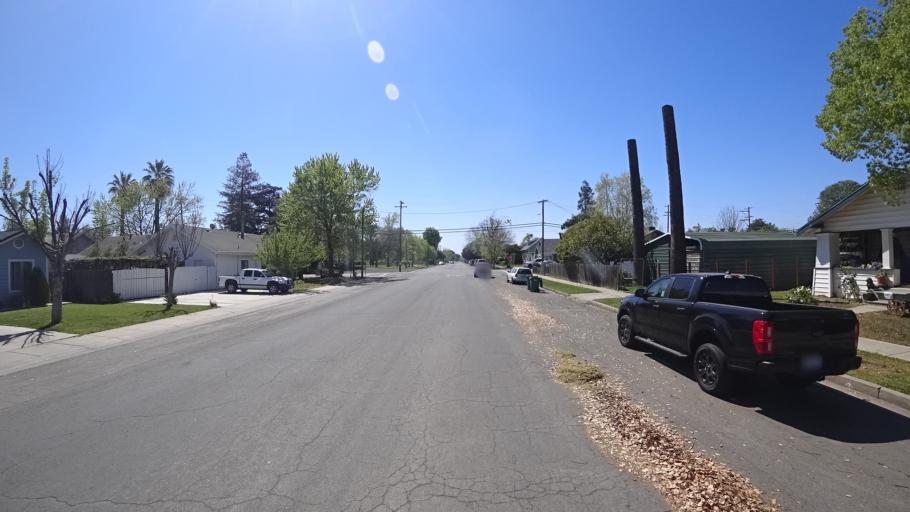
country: US
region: California
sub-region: Glenn County
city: Willows
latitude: 39.5210
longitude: -122.2046
